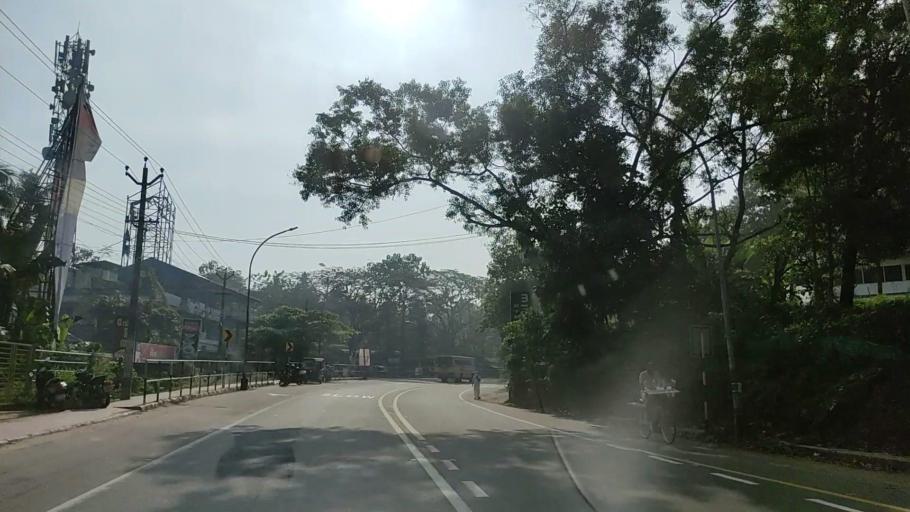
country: IN
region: Kerala
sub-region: Kollam
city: Punalur
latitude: 8.9820
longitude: 76.8094
